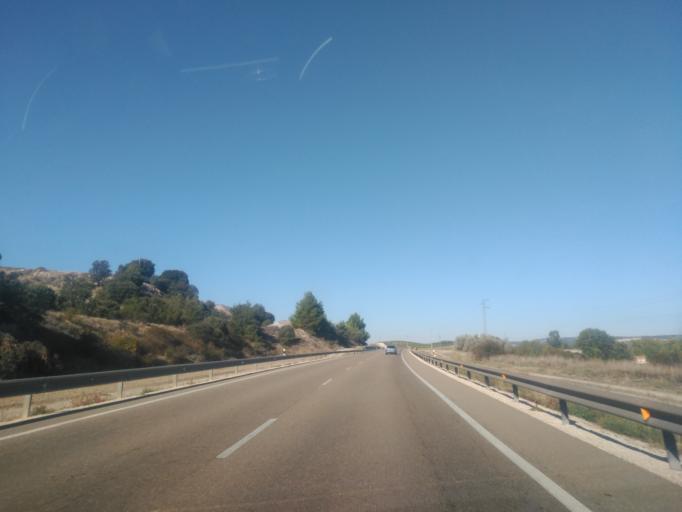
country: ES
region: Castille and Leon
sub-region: Provincia de Valladolid
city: Quintanilla de Arriba
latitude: 41.6229
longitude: -4.2520
